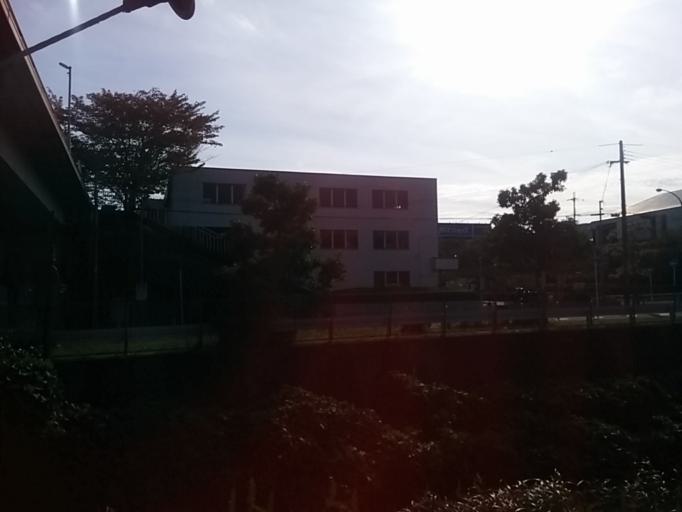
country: JP
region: Nara
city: Nara-shi
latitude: 34.7235
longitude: 135.7920
